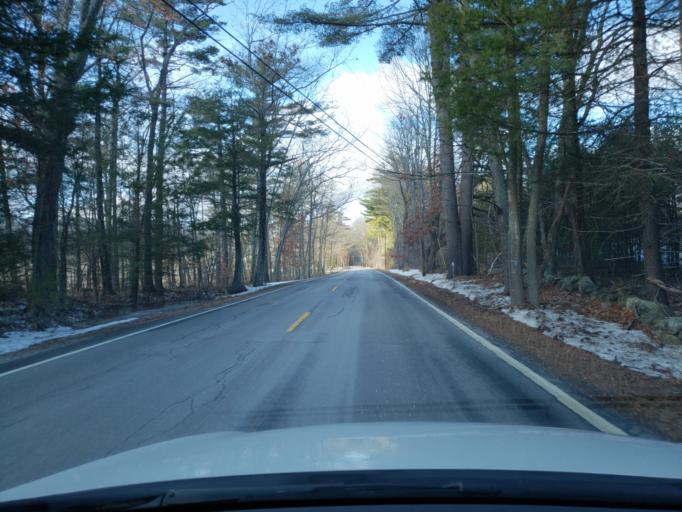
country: US
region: New Hampshire
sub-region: Hillsborough County
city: New Boston
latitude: 42.9951
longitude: -71.7488
